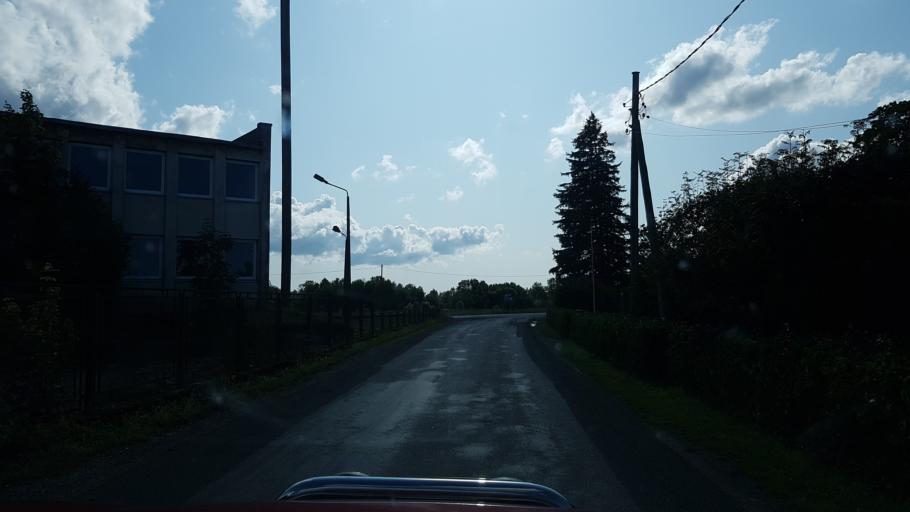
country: EE
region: Harju
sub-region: Paldiski linn
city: Paldiski
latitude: 59.2300
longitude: 24.0025
